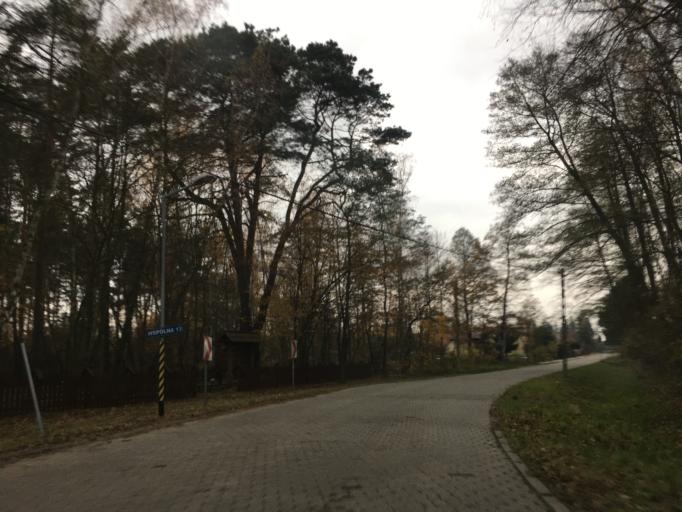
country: PL
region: Masovian Voivodeship
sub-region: Powiat piaseczynski
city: Lesznowola
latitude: 52.0428
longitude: 20.9358
